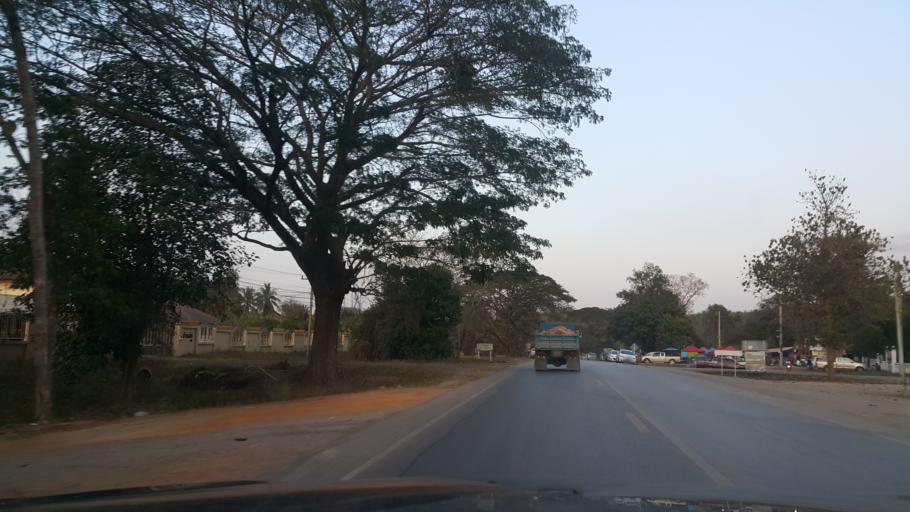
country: TH
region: Loei
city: Loei
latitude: 17.4816
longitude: 101.6804
